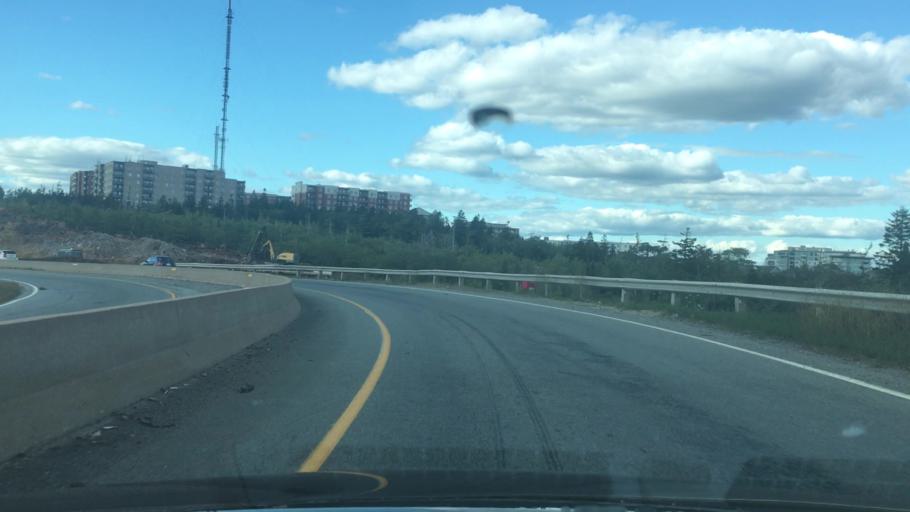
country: CA
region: Nova Scotia
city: Dartmouth
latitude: 44.6446
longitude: -63.6548
